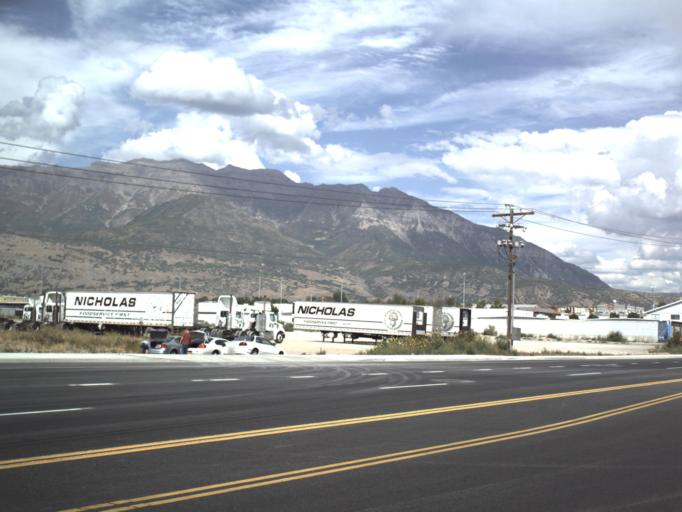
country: US
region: Utah
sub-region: Utah County
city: Lindon
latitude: 40.3118
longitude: -111.7362
